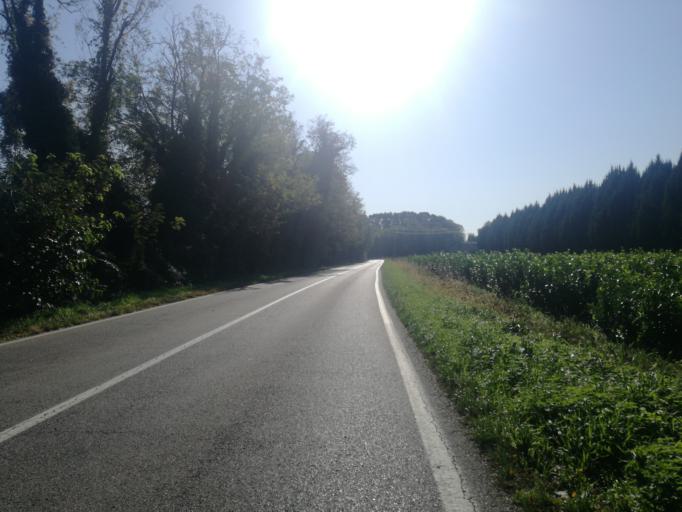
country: IT
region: Lombardy
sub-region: Provincia di Monza e Brianza
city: Cornate d'Adda
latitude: 45.6345
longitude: 9.4899
